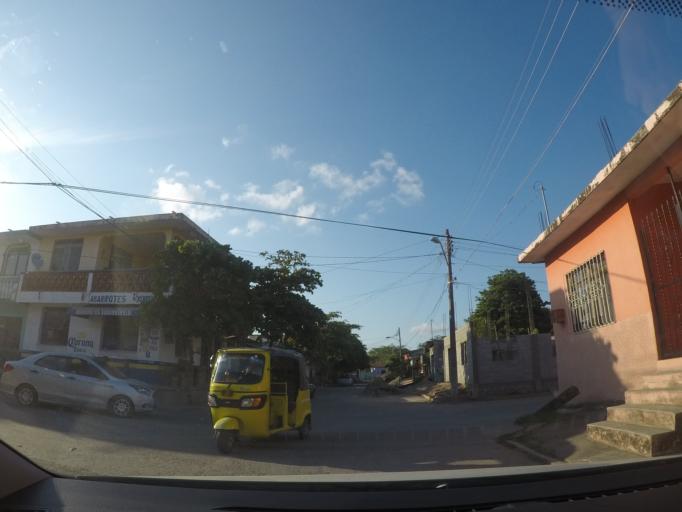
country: MX
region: Oaxaca
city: Juchitan de Zaragoza
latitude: 16.4394
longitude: -95.0266
